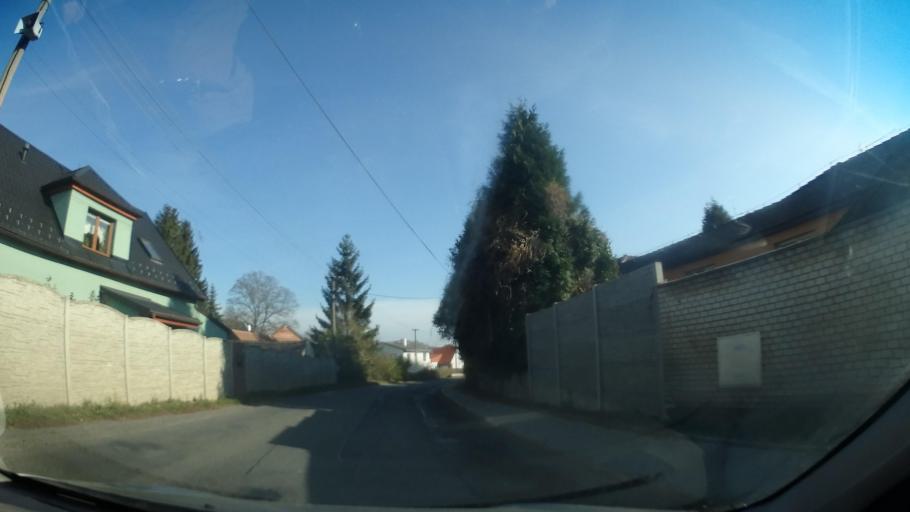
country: CZ
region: Central Bohemia
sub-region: Okres Praha-Vychod
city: Strancice
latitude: 49.9598
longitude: 14.6819
